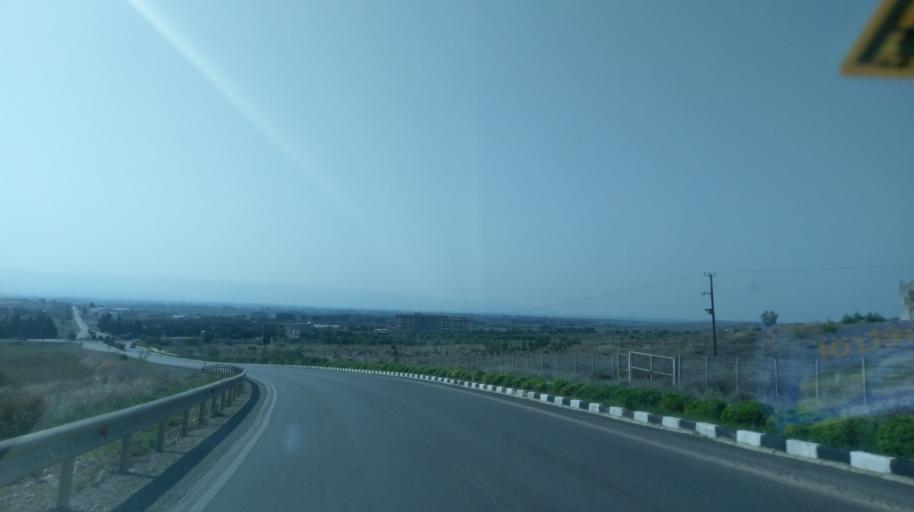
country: CY
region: Lefkosia
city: Morfou
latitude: 35.2436
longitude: 33.0298
